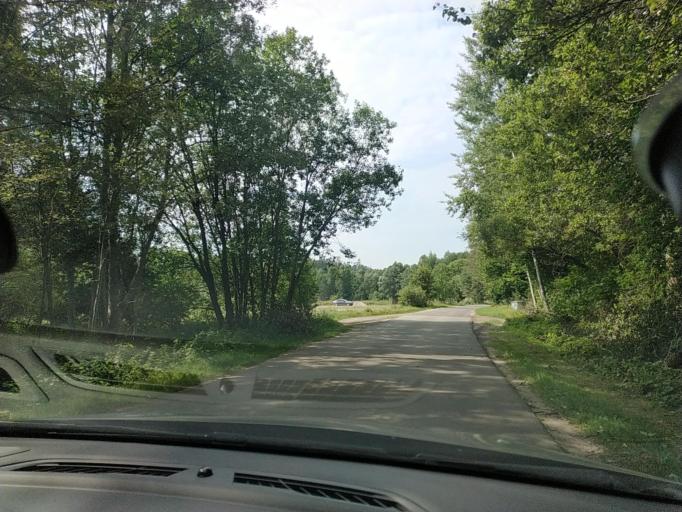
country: LT
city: Nemencine
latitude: 54.8468
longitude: 25.4563
